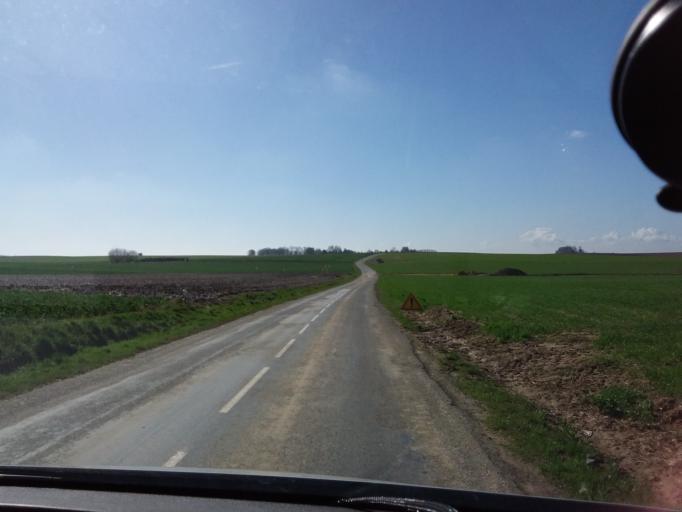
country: FR
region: Picardie
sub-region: Departement de l'Aisne
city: Montcornet
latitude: 49.7685
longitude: 4.0061
